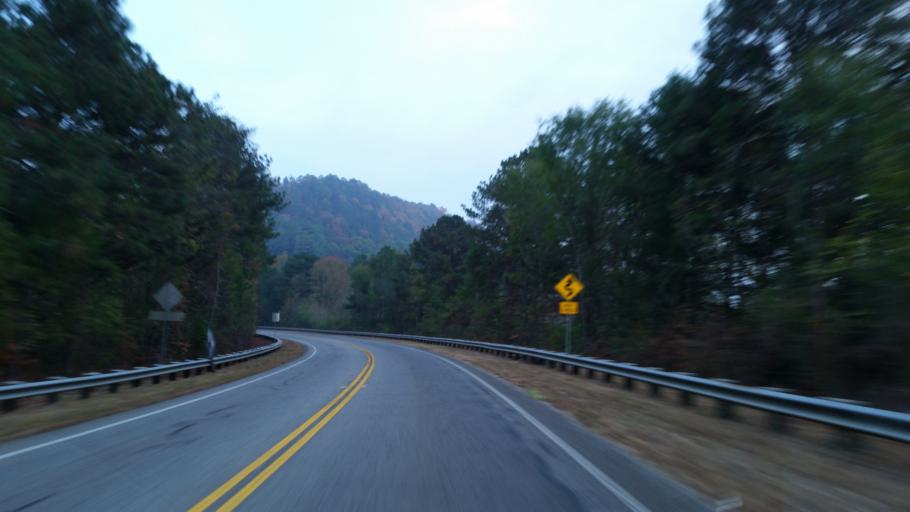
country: US
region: Georgia
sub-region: Murray County
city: Chatsworth
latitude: 34.5864
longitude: -84.6635
